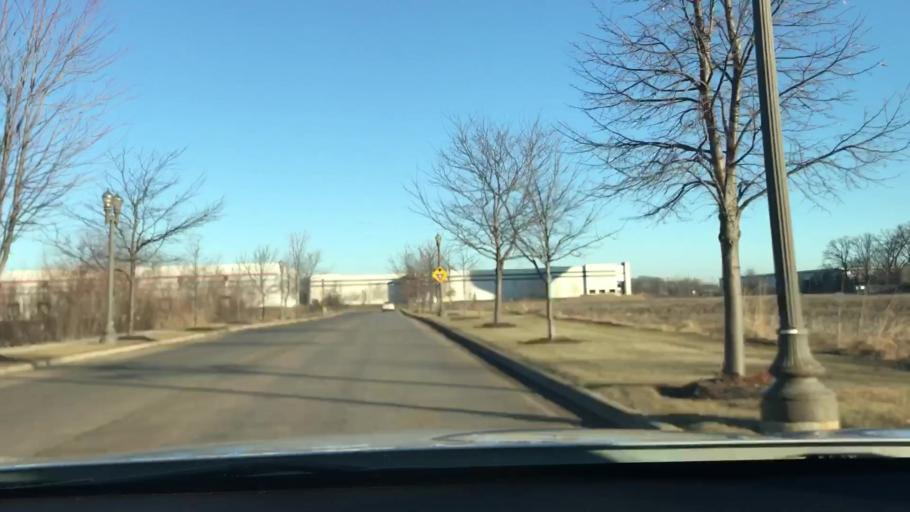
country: US
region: Illinois
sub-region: Kane County
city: Gilberts
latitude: 42.0728
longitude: -88.3467
